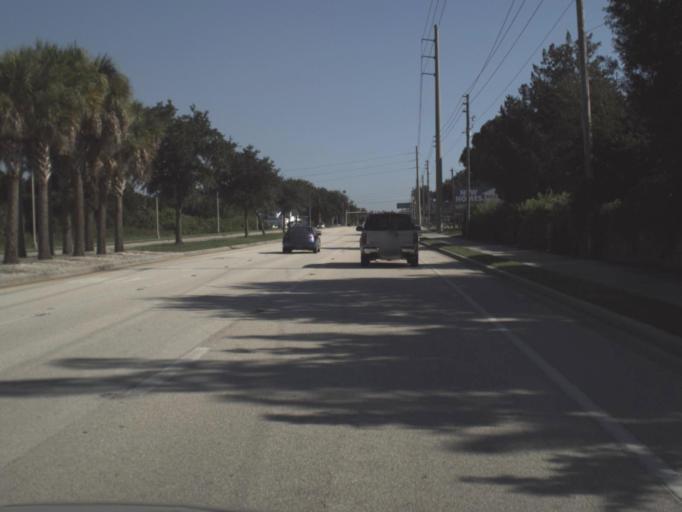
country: US
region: Florida
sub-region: Sarasota County
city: Englewood
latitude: 27.0089
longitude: -82.3819
